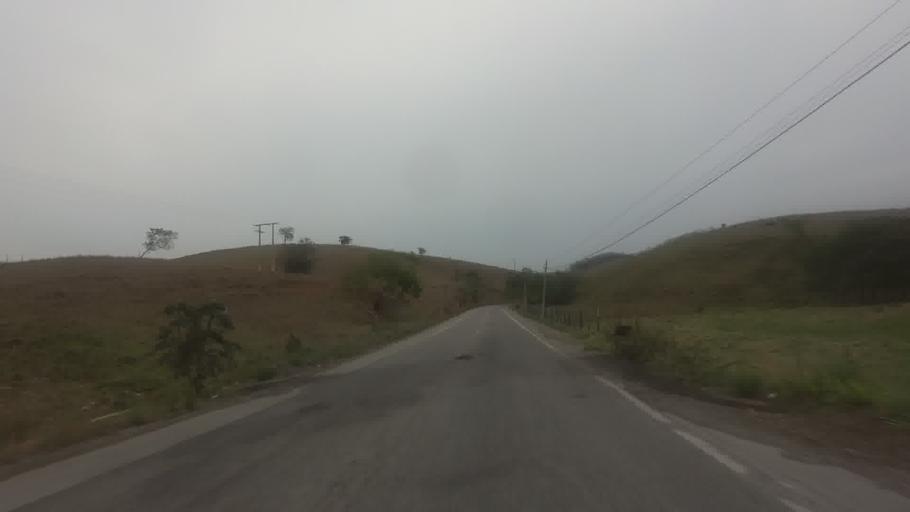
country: BR
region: Rio de Janeiro
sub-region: Santo Antonio De Padua
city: Santo Antonio de Padua
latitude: -21.6481
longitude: -42.2875
